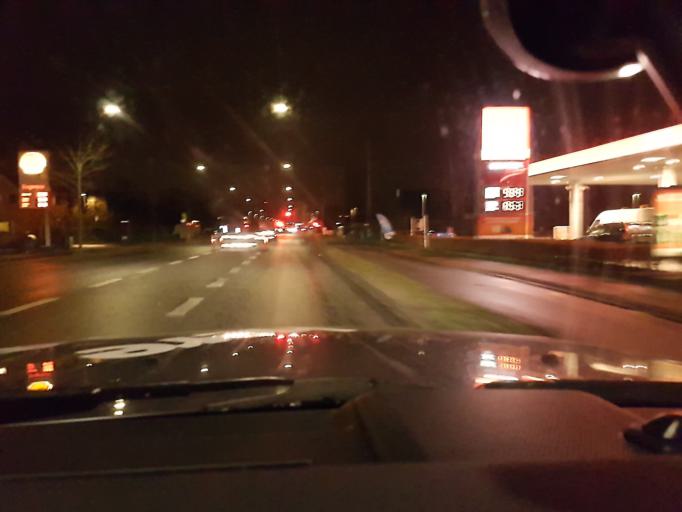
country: DK
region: Capital Region
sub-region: Tarnby Kommune
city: Tarnby
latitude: 55.6397
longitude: 12.5990
